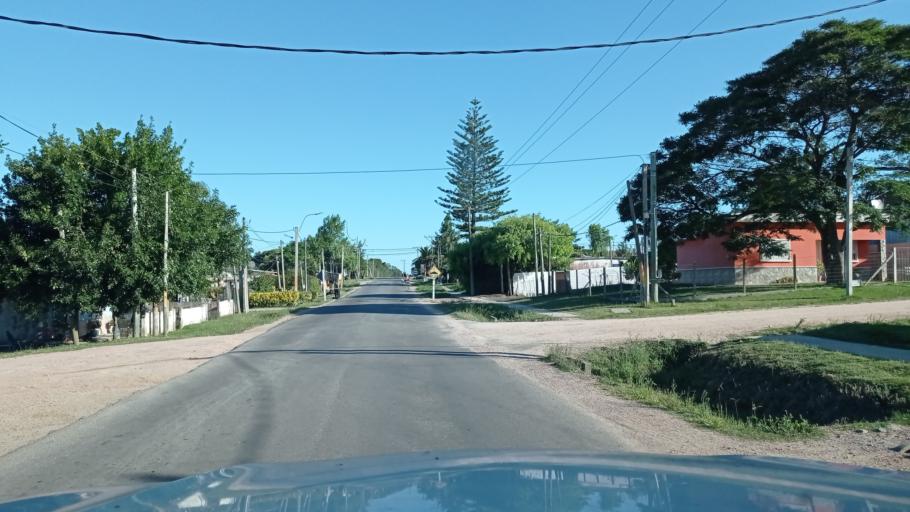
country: UY
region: Canelones
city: Colonia Nicolich
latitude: -34.8212
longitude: -56.0042
